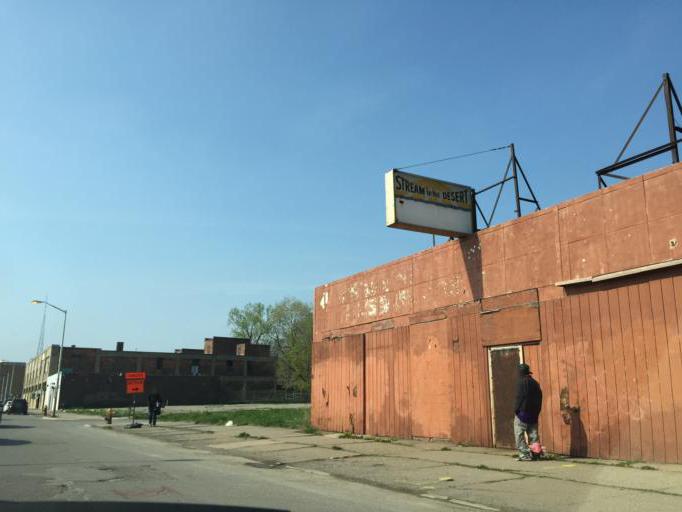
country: US
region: Michigan
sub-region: Wayne County
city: Detroit
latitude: 42.3425
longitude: -83.0589
